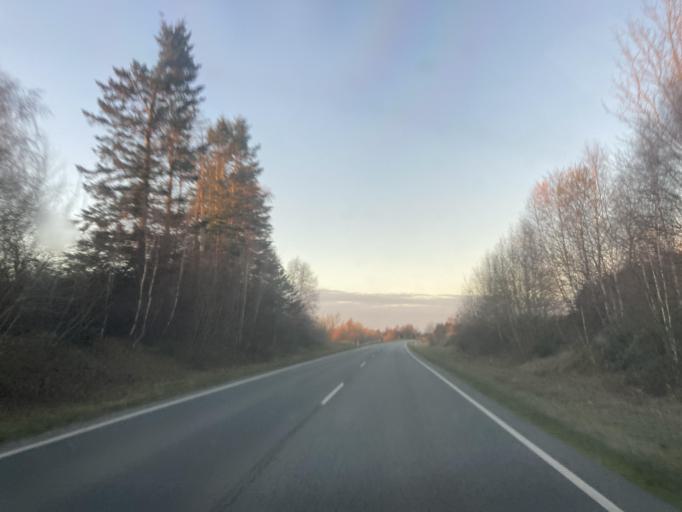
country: DK
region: Capital Region
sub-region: Gribskov Kommune
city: Graested
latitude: 56.0526
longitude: 12.2782
